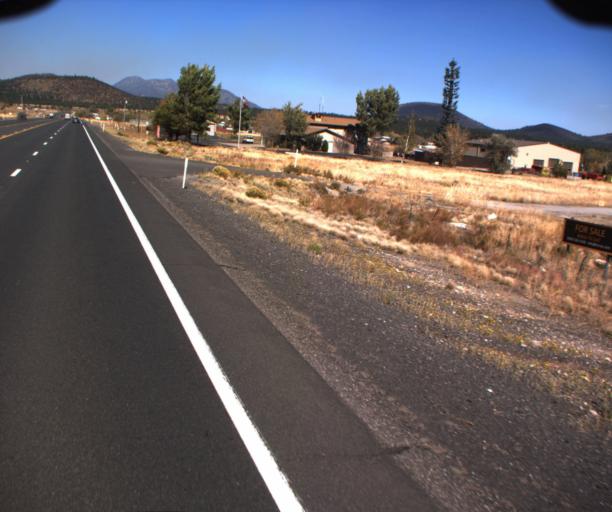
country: US
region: Arizona
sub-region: Coconino County
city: Flagstaff
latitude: 35.3097
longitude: -111.5426
